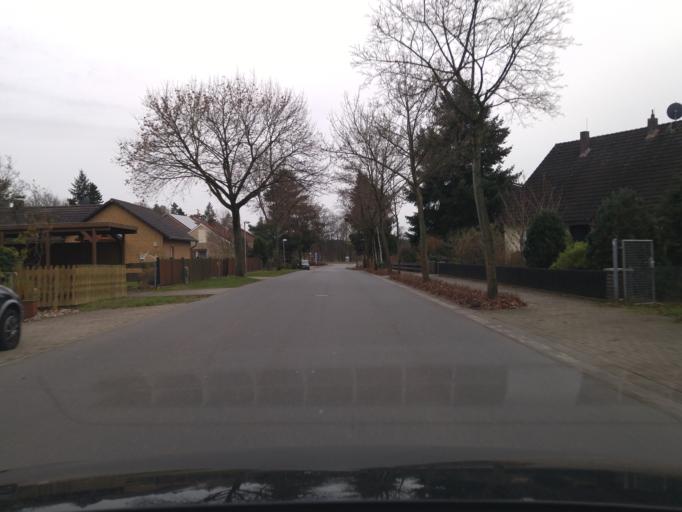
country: DE
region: Lower Saxony
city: Winsen
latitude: 52.6774
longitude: 9.9214
